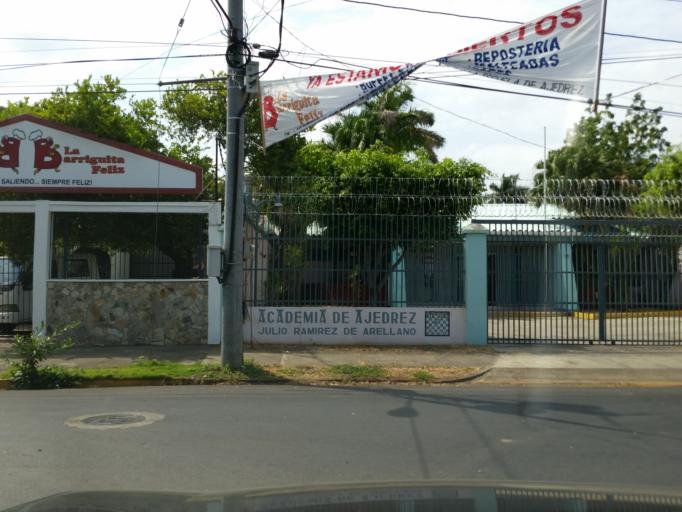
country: NI
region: Managua
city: Managua
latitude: 12.1373
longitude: -86.2783
